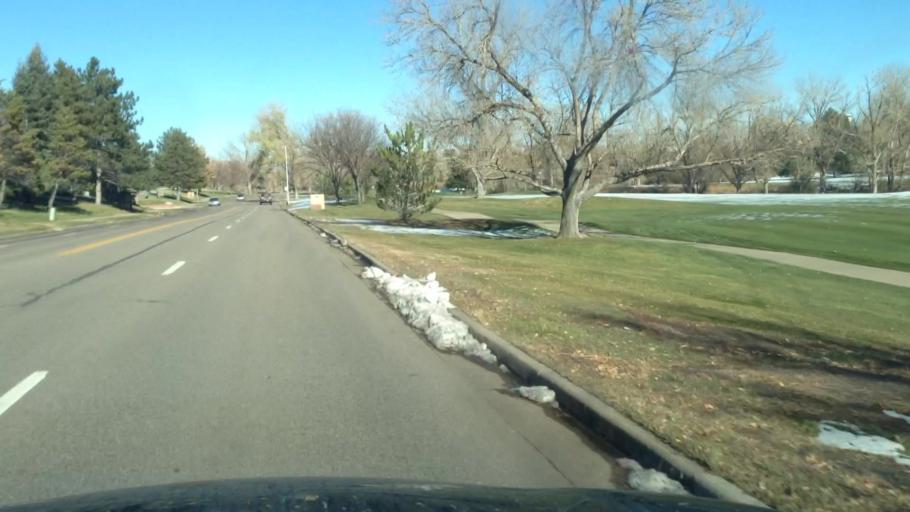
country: US
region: Colorado
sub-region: Douglas County
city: Meridian
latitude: 39.5691
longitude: -104.8605
